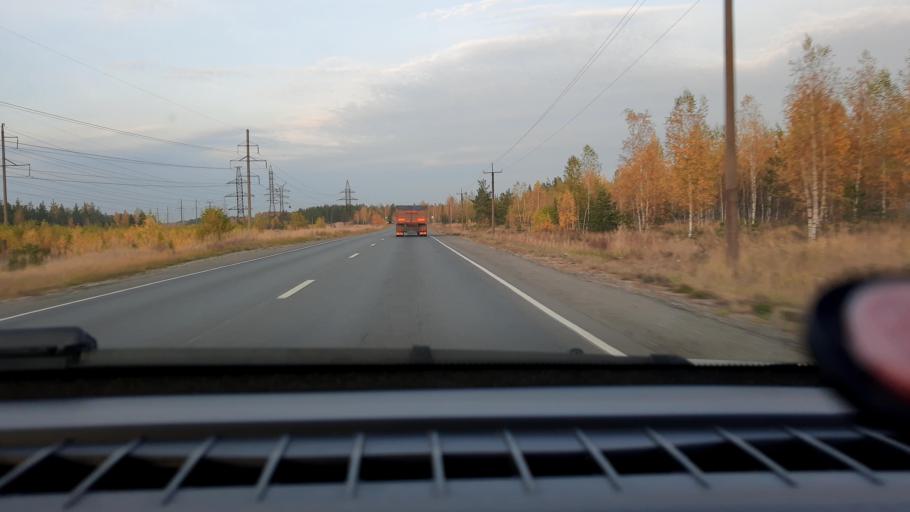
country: RU
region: Nizjnij Novgorod
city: Babino
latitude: 56.3347
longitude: 43.5731
